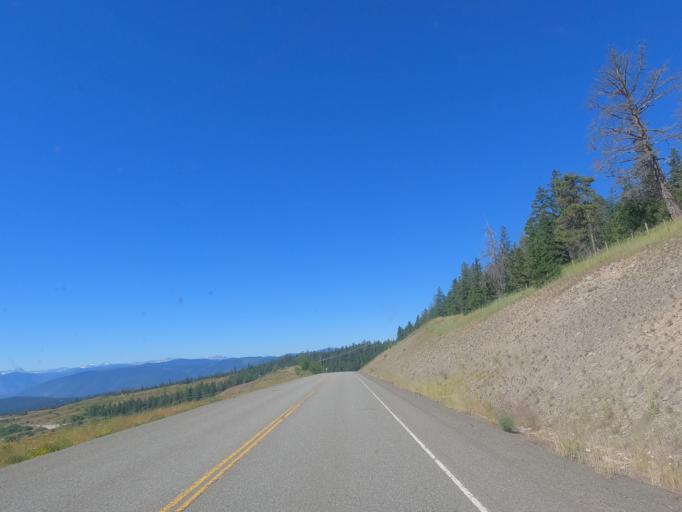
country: CA
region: British Columbia
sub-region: Thompson-Nicola Regional District
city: Ashcroft
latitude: 50.5701
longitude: -121.1828
